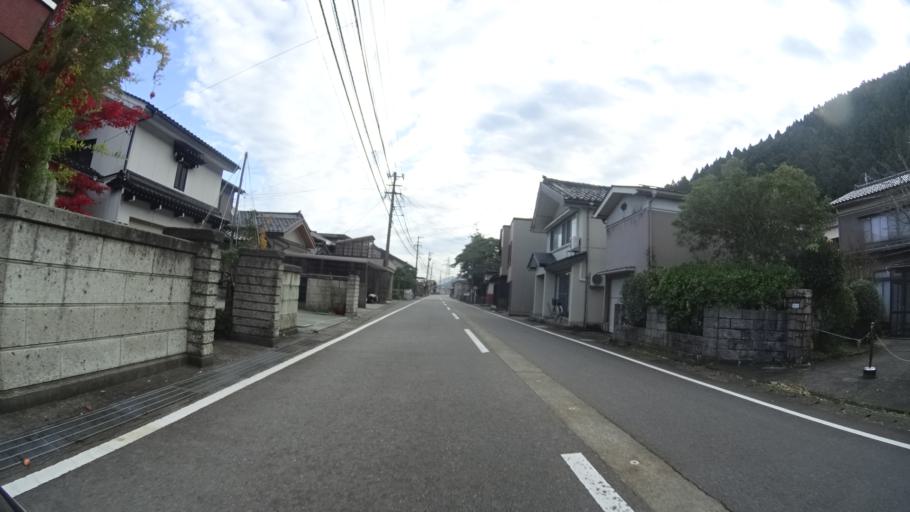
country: JP
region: Toyama
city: Nyuzen
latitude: 36.9776
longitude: 137.6296
